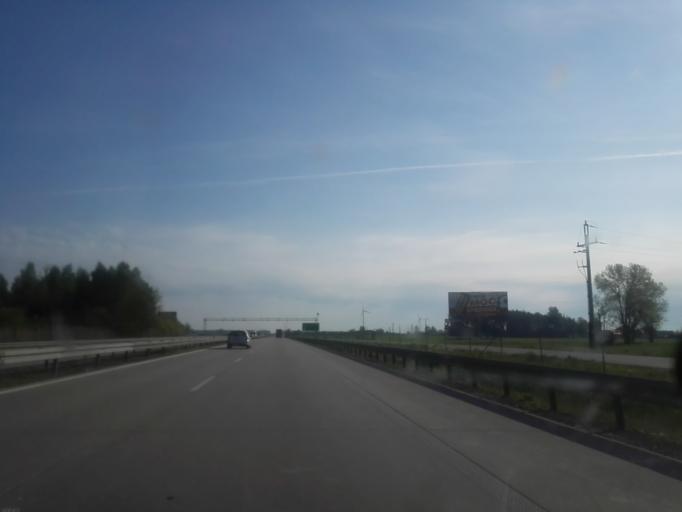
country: PL
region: Lodz Voivodeship
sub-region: Powiat piotrkowski
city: Wolborz
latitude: 51.4664
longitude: 19.7906
